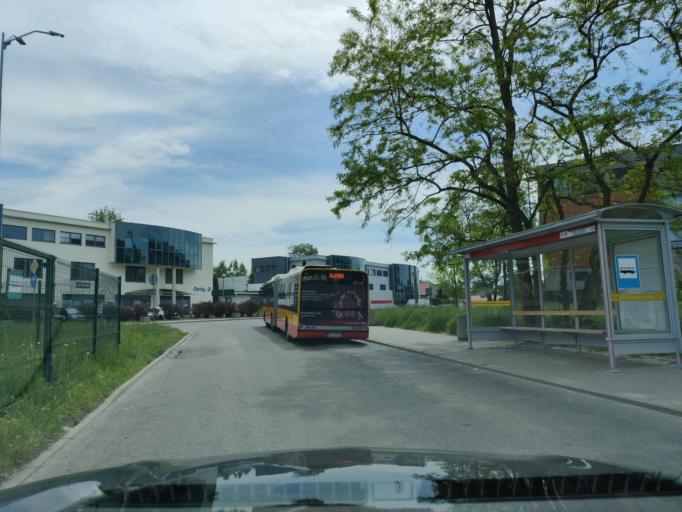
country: PL
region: Masovian Voivodeship
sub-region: Warszawa
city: Mokotow
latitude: 52.1585
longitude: 21.0023
